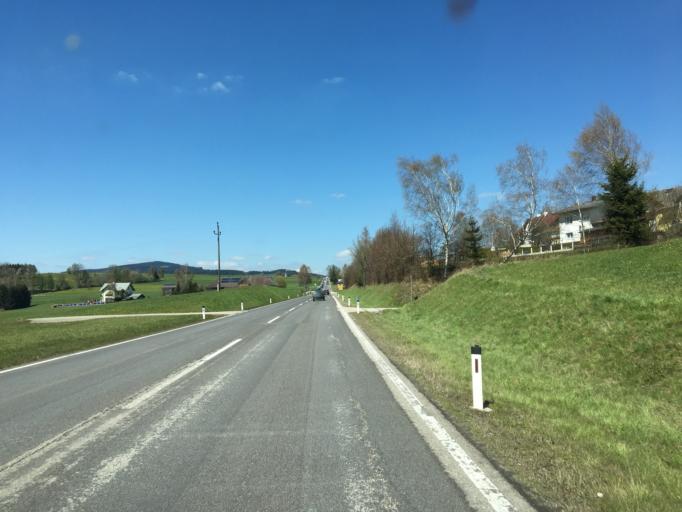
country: AT
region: Upper Austria
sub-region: Politischer Bezirk Urfahr-Umgebung
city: Bad Leonfelden
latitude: 48.5036
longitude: 14.2952
